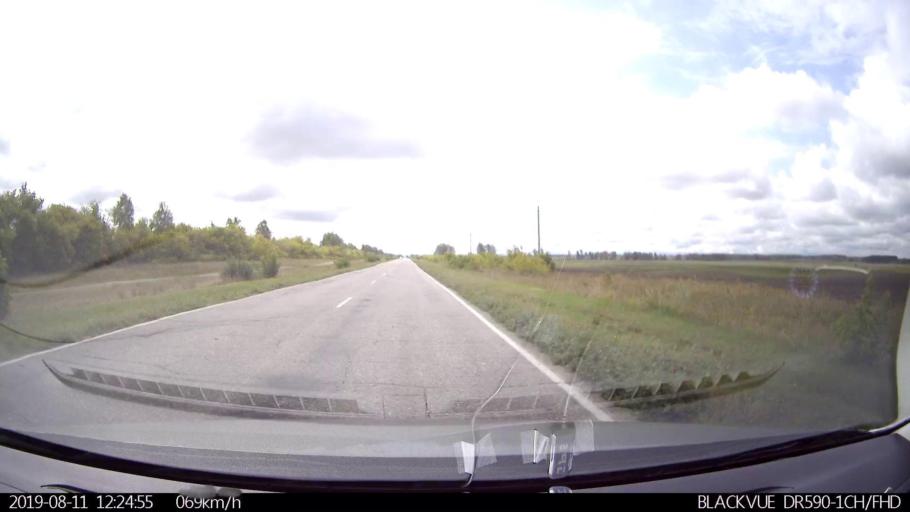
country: RU
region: Ulyanovsk
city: Ignatovka
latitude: 53.8787
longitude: 47.9446
